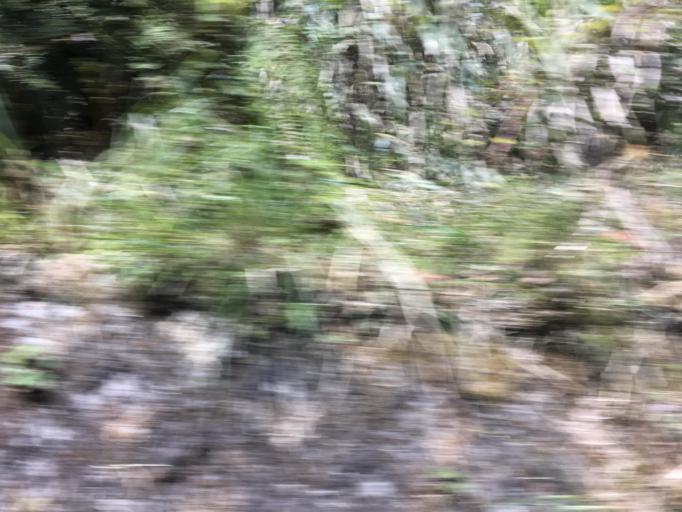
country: TW
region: Taiwan
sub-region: Yilan
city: Yilan
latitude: 24.5197
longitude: 121.5220
